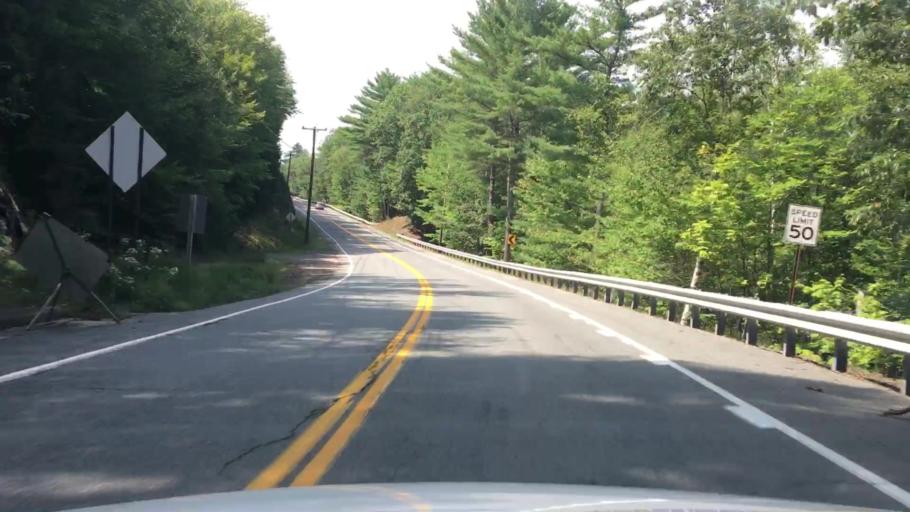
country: US
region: Maine
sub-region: Oxford County
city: Dixfield
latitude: 44.5300
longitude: -70.4680
